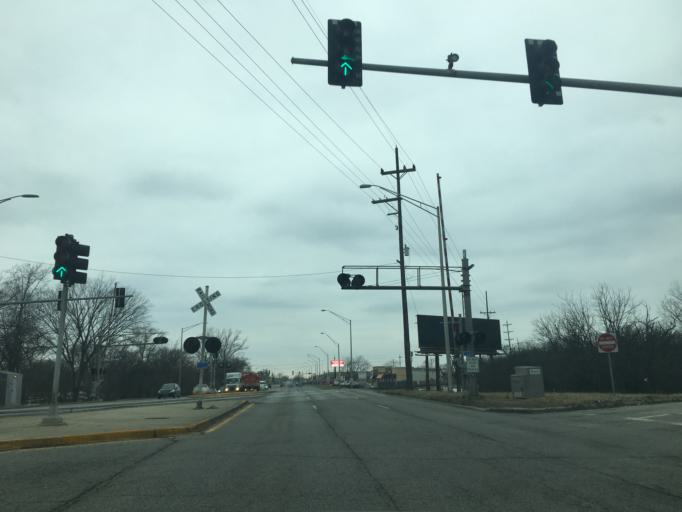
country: US
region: Illinois
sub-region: Cook County
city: North Riverside
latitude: 41.8501
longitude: -87.8289
